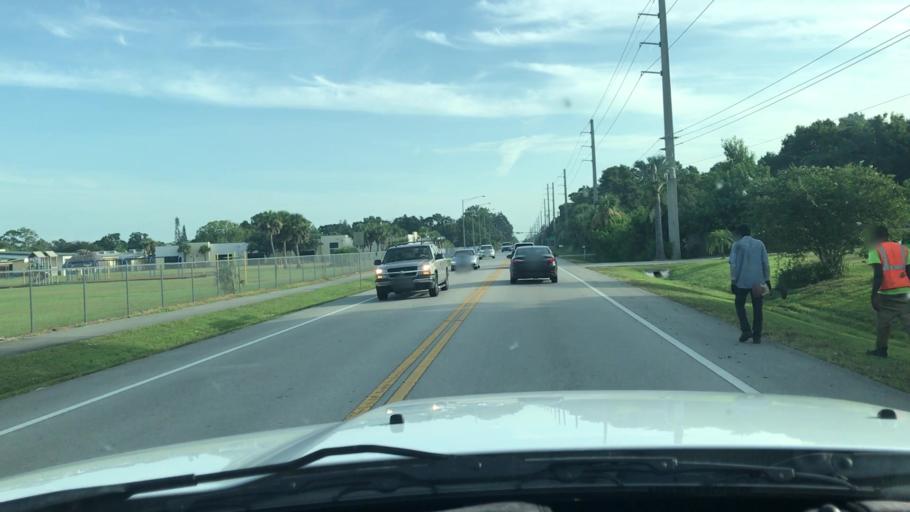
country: US
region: Florida
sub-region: Indian River County
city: Vero Beach South
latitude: 27.6057
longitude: -80.4140
